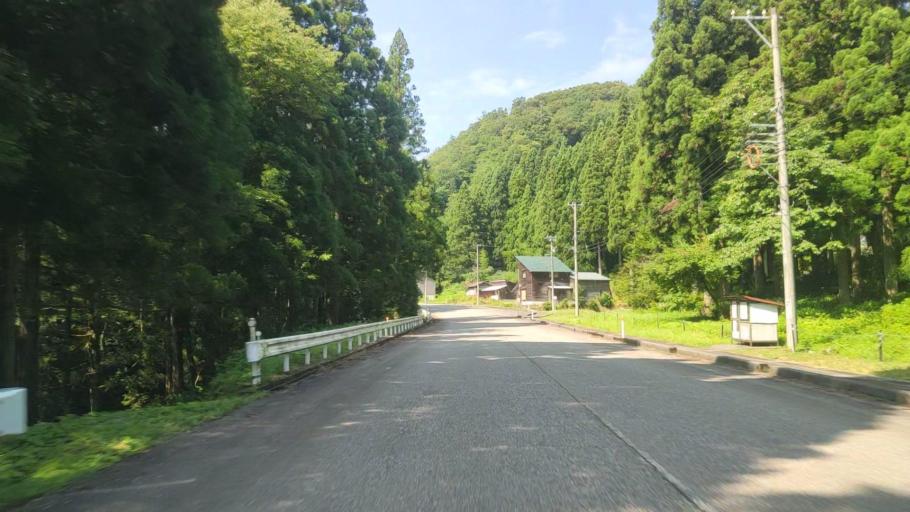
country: JP
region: Ishikawa
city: Komatsu
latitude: 36.3138
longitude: 136.5305
